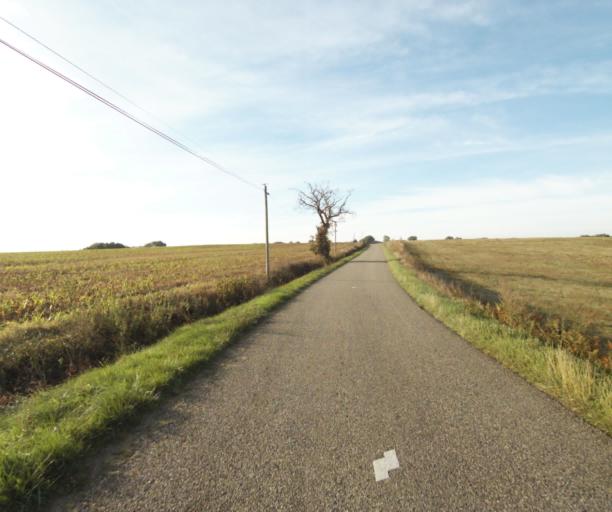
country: FR
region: Midi-Pyrenees
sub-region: Departement de la Haute-Garonne
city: Villemur-sur-Tarn
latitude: 43.9150
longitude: 1.4949
